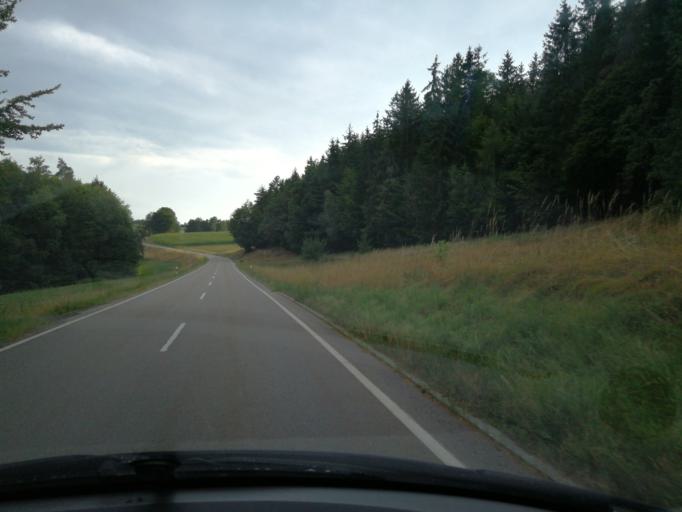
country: DE
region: Bavaria
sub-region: Lower Bavaria
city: Falkenfels
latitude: 49.0448
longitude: 12.6084
